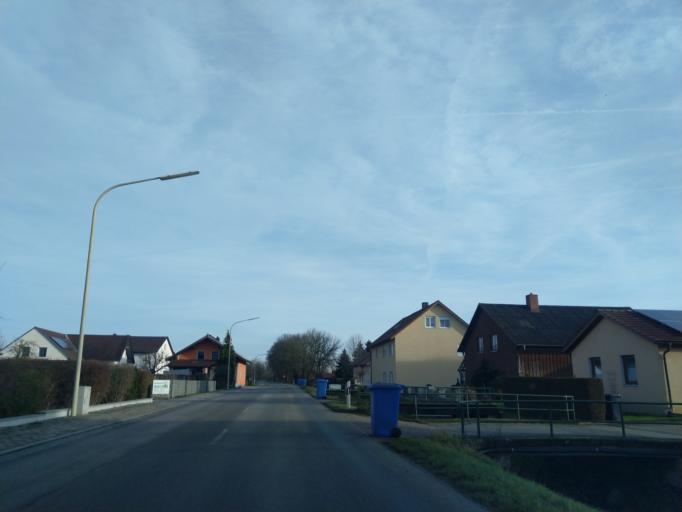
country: DE
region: Bavaria
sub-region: Lower Bavaria
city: Buchhofen
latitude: 48.6975
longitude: 12.9290
